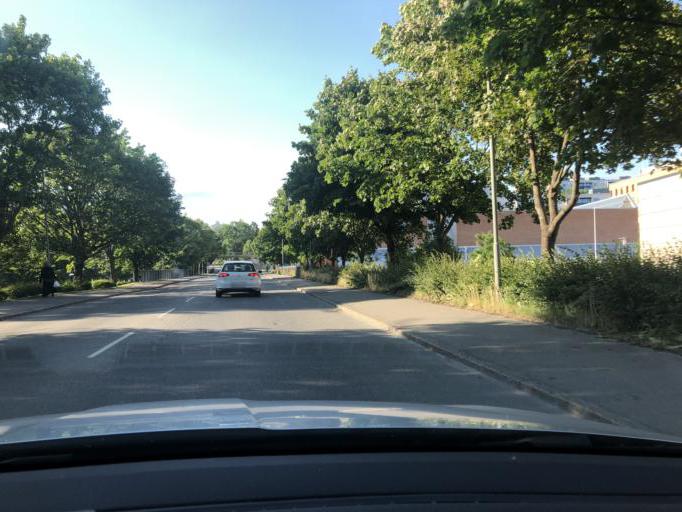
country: SE
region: Stockholm
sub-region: Huddinge Kommun
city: Segeltorp
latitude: 59.2752
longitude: 17.9033
